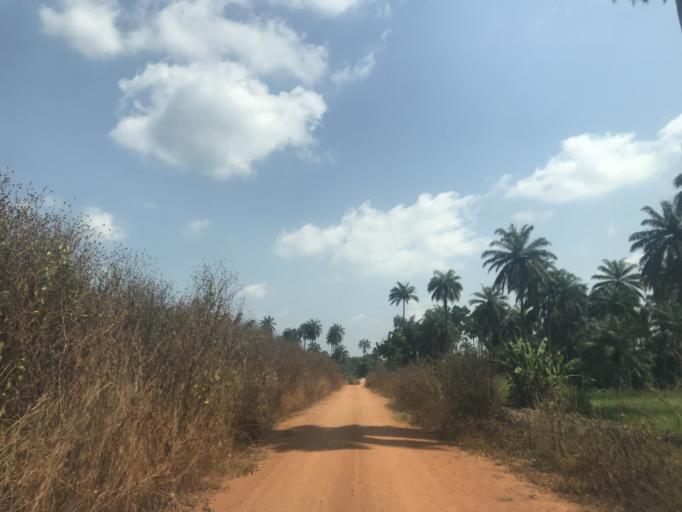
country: NG
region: Osun
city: Oke Mesi
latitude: 7.8934
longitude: 4.8742
